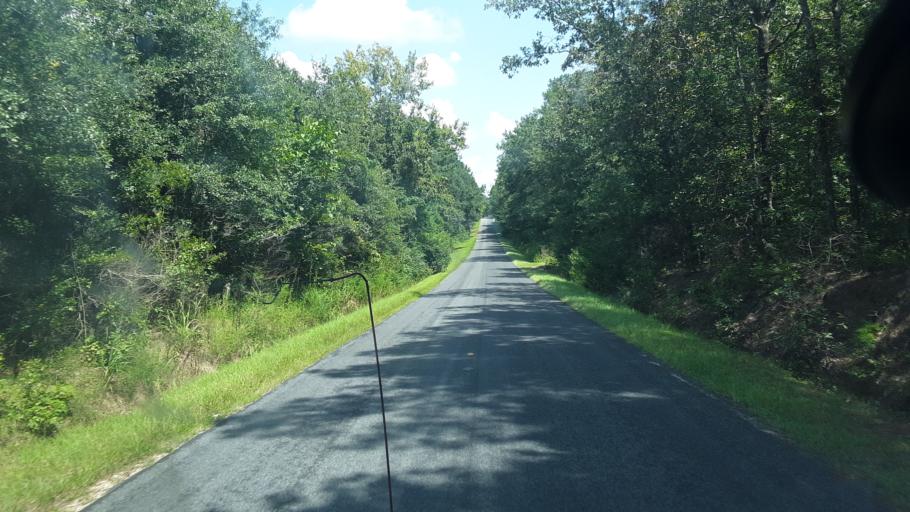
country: US
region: South Carolina
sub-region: Calhoun County
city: Oak Grove
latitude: 33.6912
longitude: -80.9665
